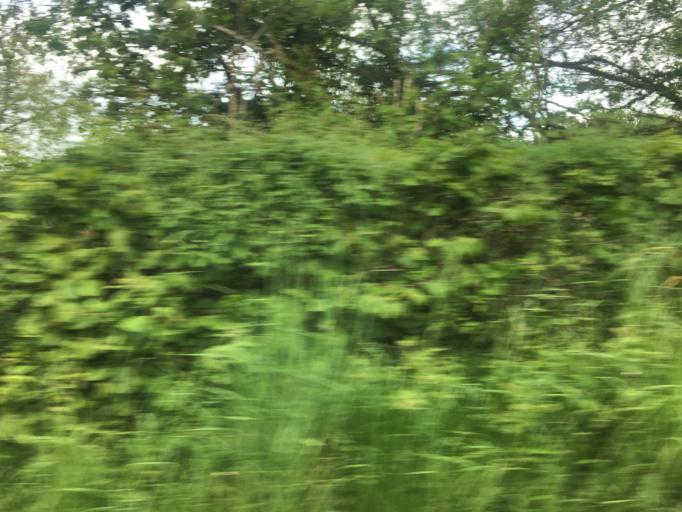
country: GB
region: Wales
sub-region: County of Ceredigion
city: Lampeter
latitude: 52.1236
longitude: -4.0779
